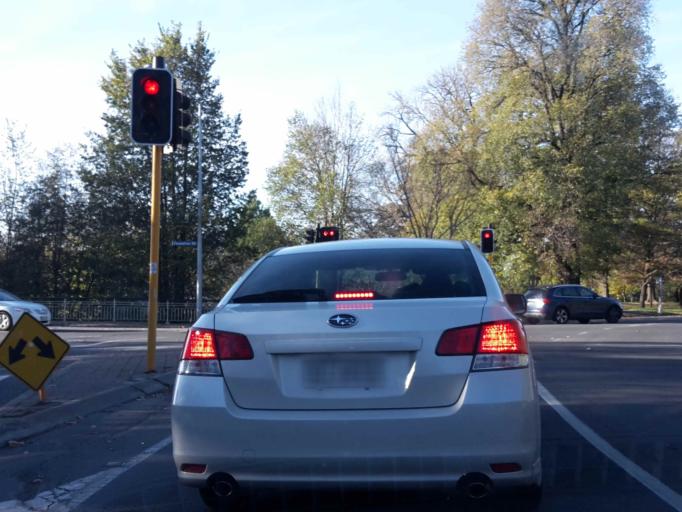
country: NZ
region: Canterbury
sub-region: Christchurch City
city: Christchurch
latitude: -43.5243
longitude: 172.6130
